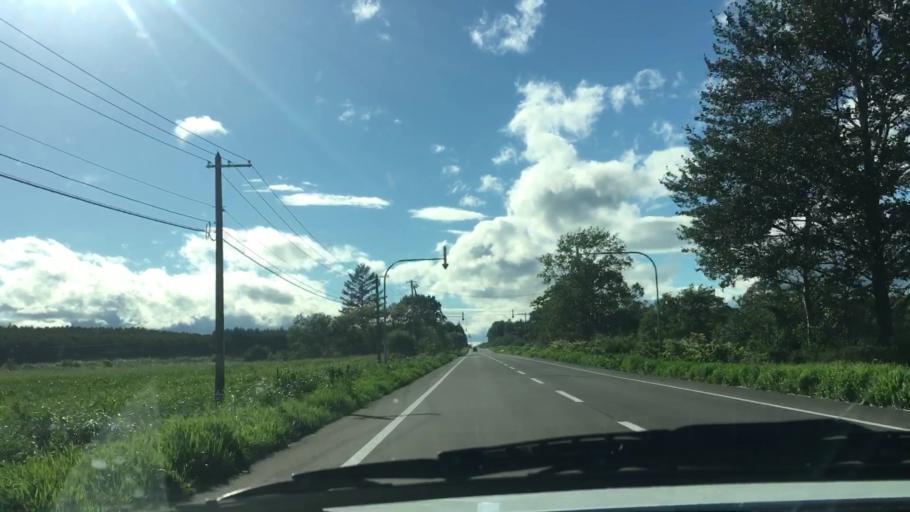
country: JP
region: Hokkaido
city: Otofuke
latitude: 43.1620
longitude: 143.1557
